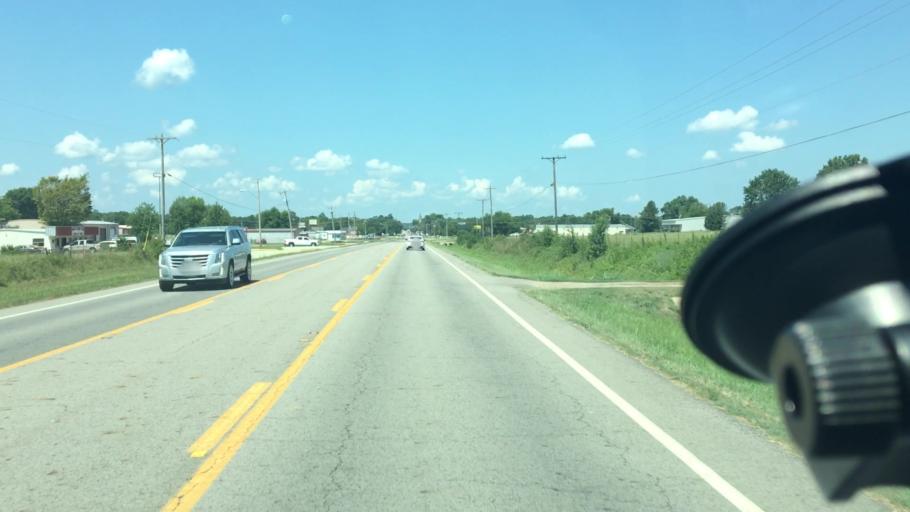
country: US
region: Arkansas
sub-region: Franklin County
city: Charleston
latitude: 35.2969
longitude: -94.0210
